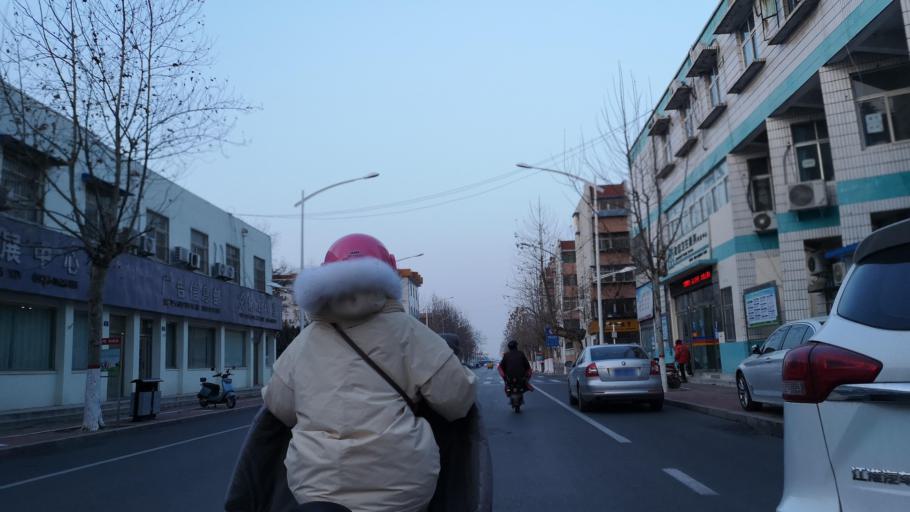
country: CN
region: Henan Sheng
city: Zhongyuanlu
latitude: 35.7765
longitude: 115.0794
